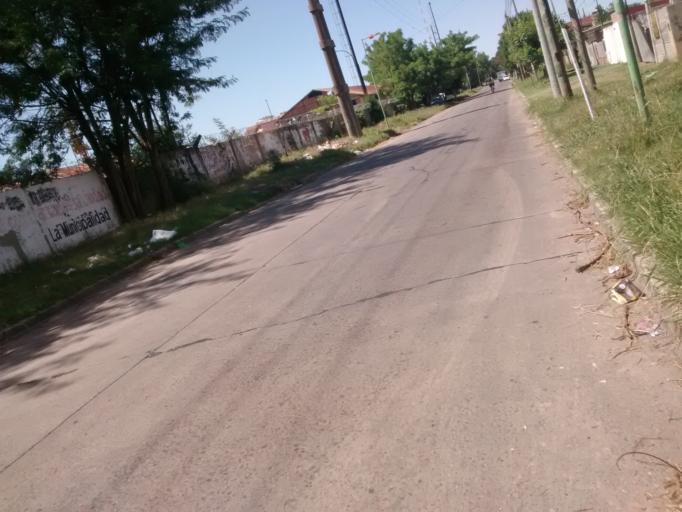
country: AR
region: Buenos Aires
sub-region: Partido de La Plata
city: La Plata
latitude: -34.9488
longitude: -57.9804
